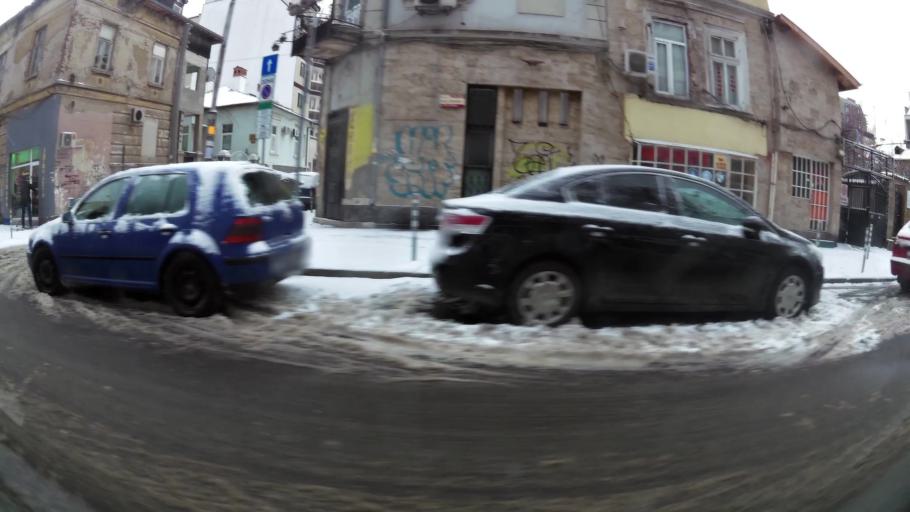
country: BG
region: Sofia-Capital
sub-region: Stolichna Obshtina
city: Sofia
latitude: 42.7026
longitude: 23.3145
